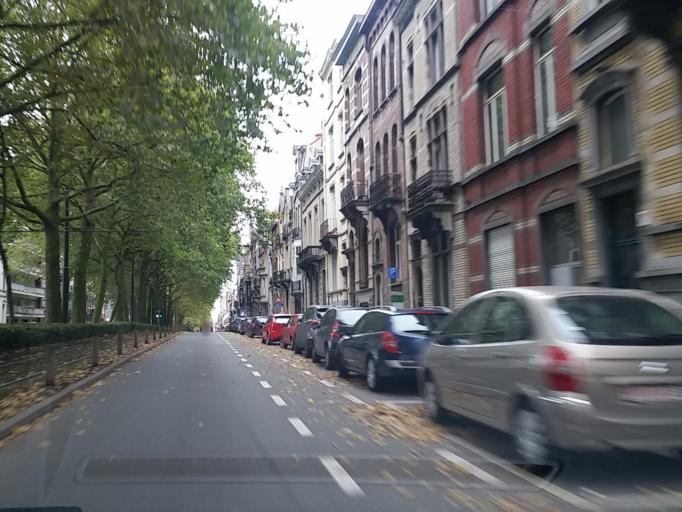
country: BE
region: Flanders
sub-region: Provincie Vlaams-Brabant
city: Drogenbos
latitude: 50.8178
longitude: 4.3255
